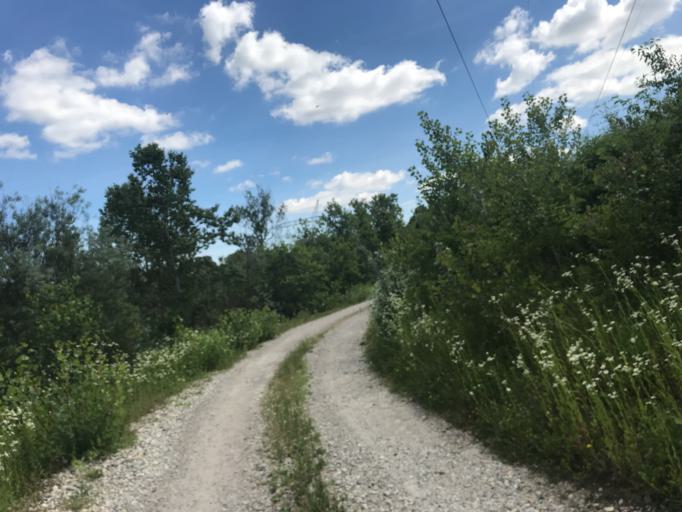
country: FR
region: Rhone-Alpes
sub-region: Departement de l'Ain
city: Thil
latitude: 45.8129
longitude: 5.0314
